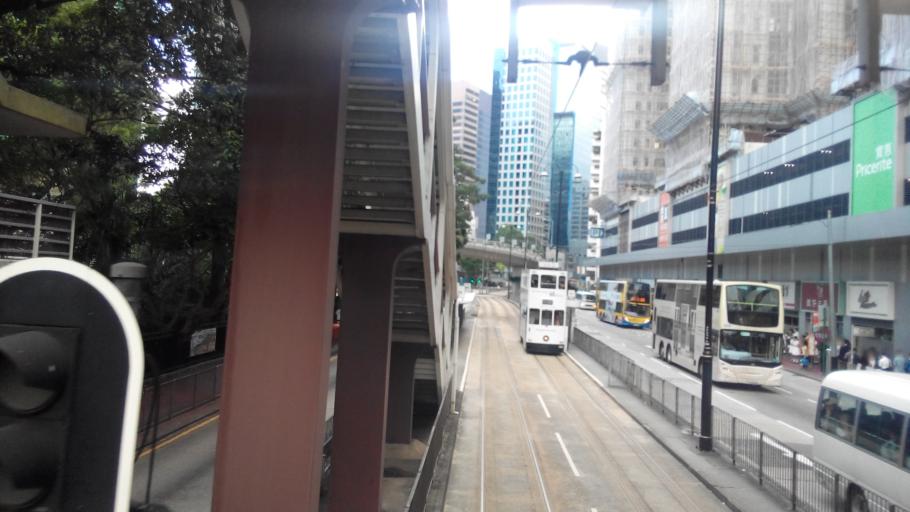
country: HK
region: Kowloon City
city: Kowloon
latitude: 22.2918
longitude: 114.2031
